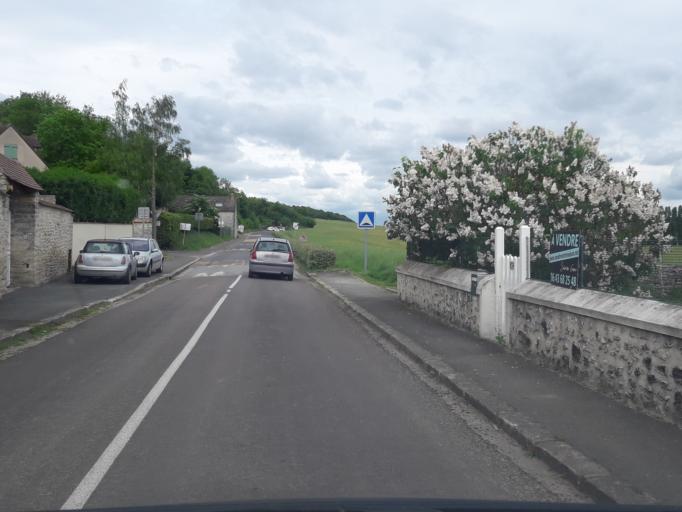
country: FR
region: Ile-de-France
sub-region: Departement de l'Essonne
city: Boissy-le-Cutte
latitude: 48.4070
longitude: 2.2651
